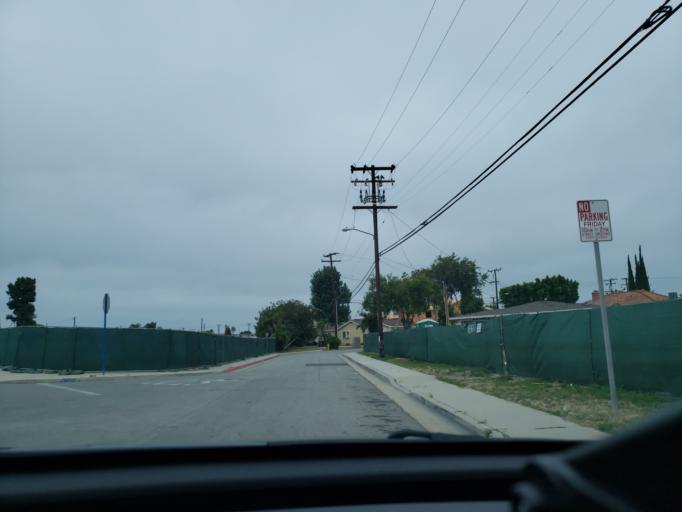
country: US
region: California
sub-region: Los Angeles County
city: Artesia
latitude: 33.8628
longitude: -118.0865
